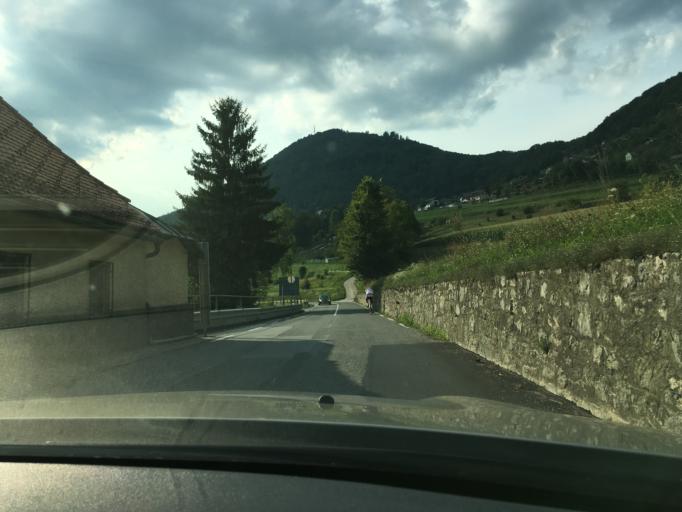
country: SI
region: Dolenjske Toplice
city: Dolenjske Toplice
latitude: 45.7800
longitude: 15.0185
